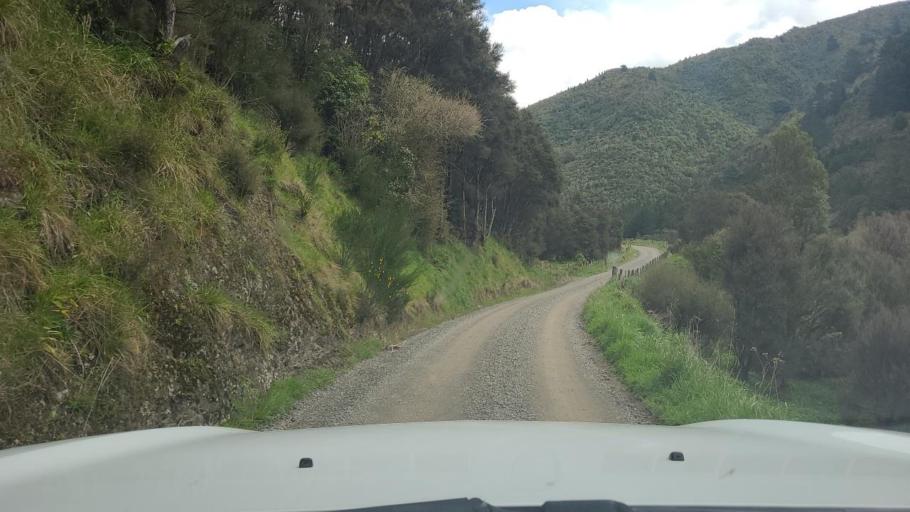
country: NZ
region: Wellington
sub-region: Masterton District
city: Masterton
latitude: -40.9348
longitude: 175.4726
